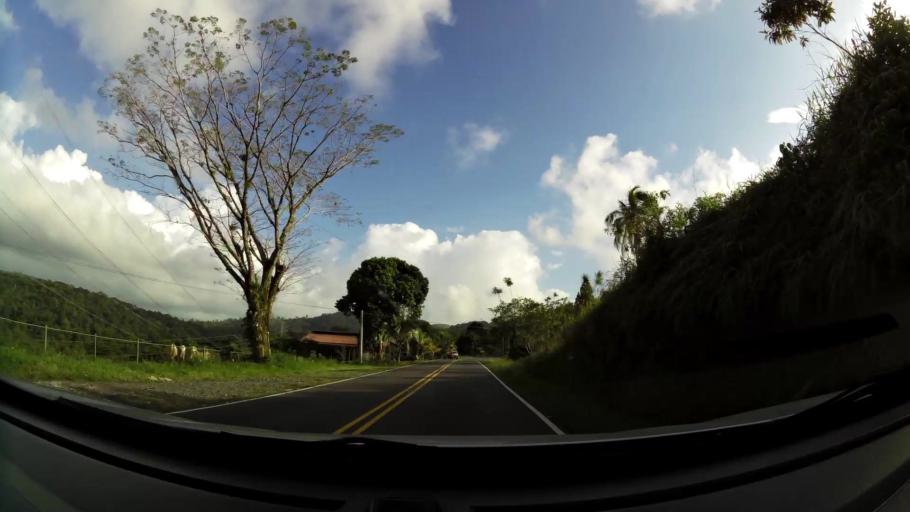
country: CR
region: Limon
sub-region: Canton de Siquirres
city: Siquirres
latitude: 10.0638
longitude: -83.5534
